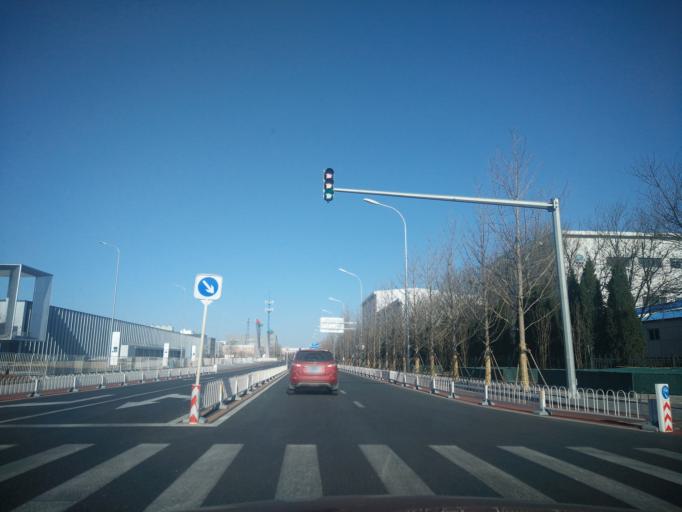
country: CN
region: Beijing
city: Jiugong
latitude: 39.7771
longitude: 116.5200
